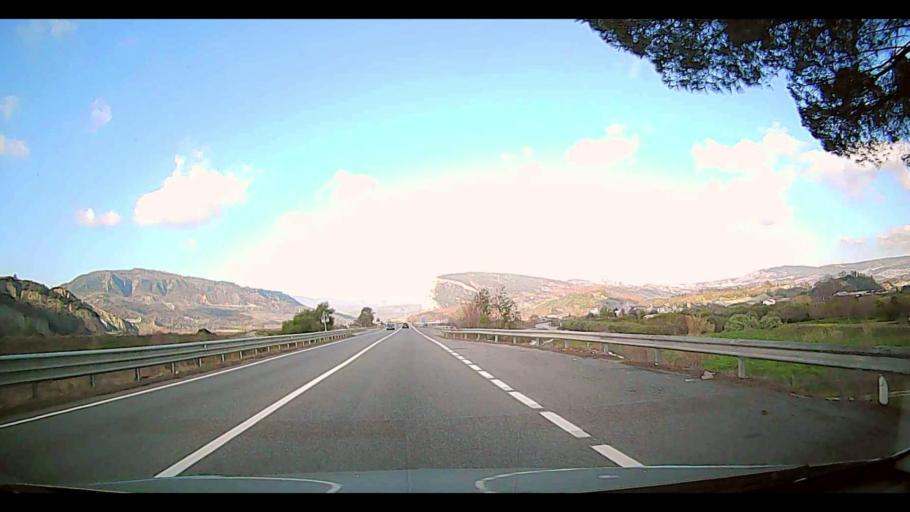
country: IT
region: Calabria
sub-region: Provincia di Crotone
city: Santa Severina
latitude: 39.1788
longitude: 16.9232
